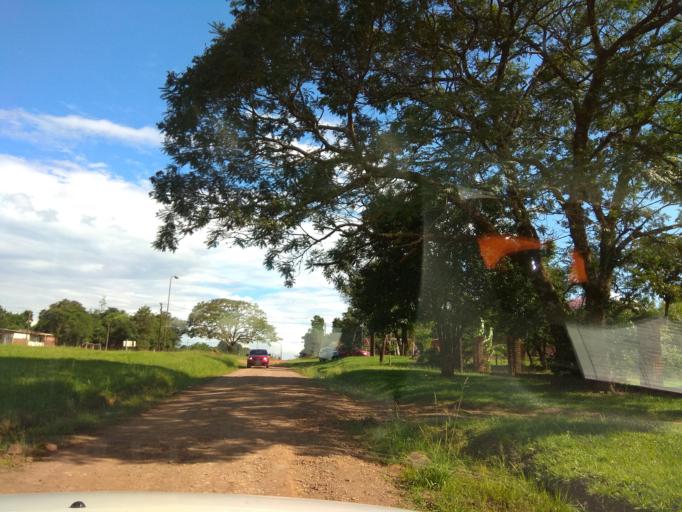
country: AR
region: Misiones
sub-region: Departamento de Candelaria
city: Candelaria
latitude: -27.4590
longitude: -55.7551
